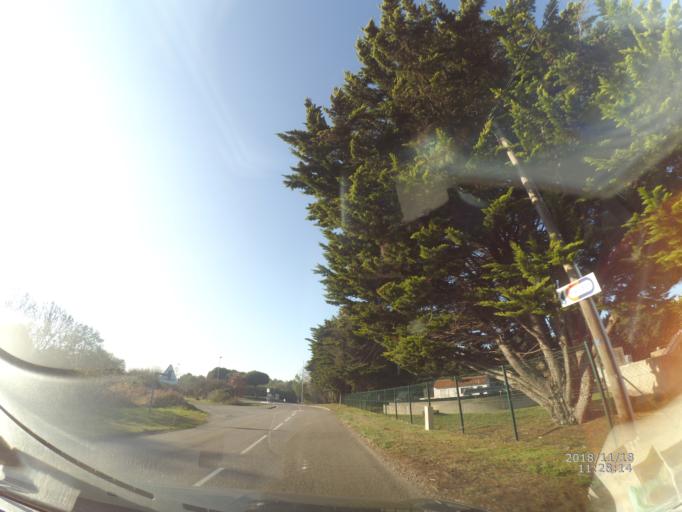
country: FR
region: Pays de la Loire
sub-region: Departement de la Loire-Atlantique
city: Saint-Michel-Chef-Chef
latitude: 47.2153
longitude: -2.1489
